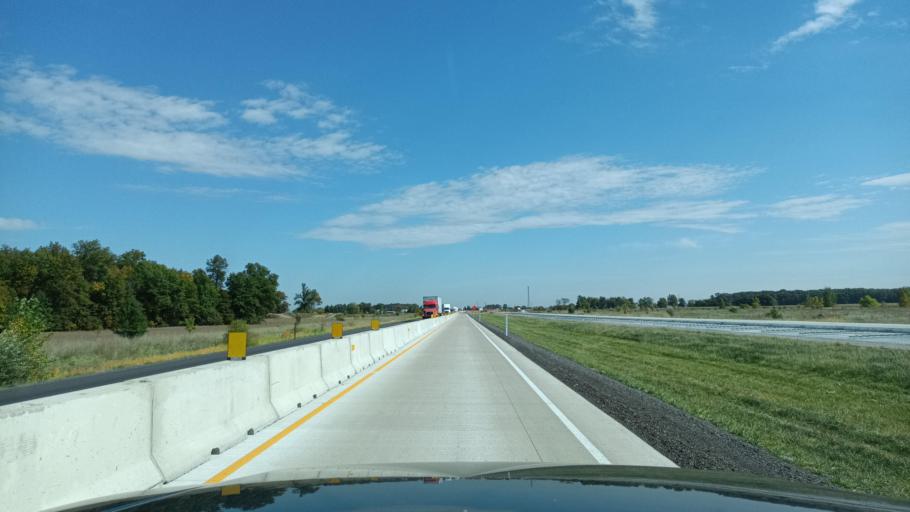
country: US
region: Indiana
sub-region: Allen County
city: Woodburn
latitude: 41.1165
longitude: -84.9174
